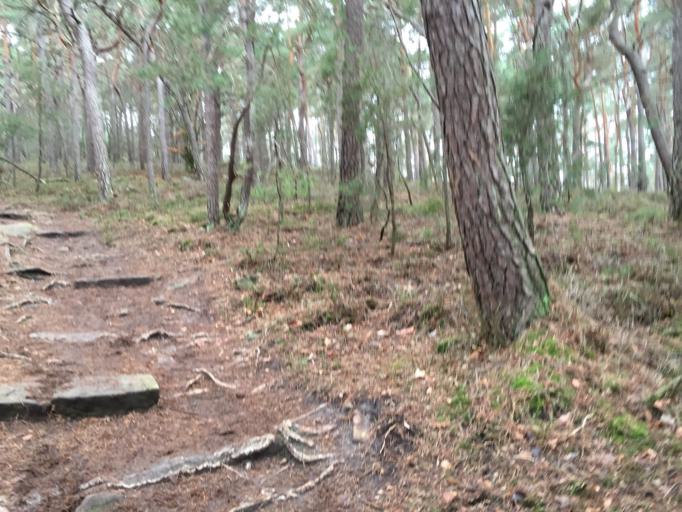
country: DE
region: Rheinland-Pfalz
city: Neustadt
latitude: 49.3361
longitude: 8.1085
